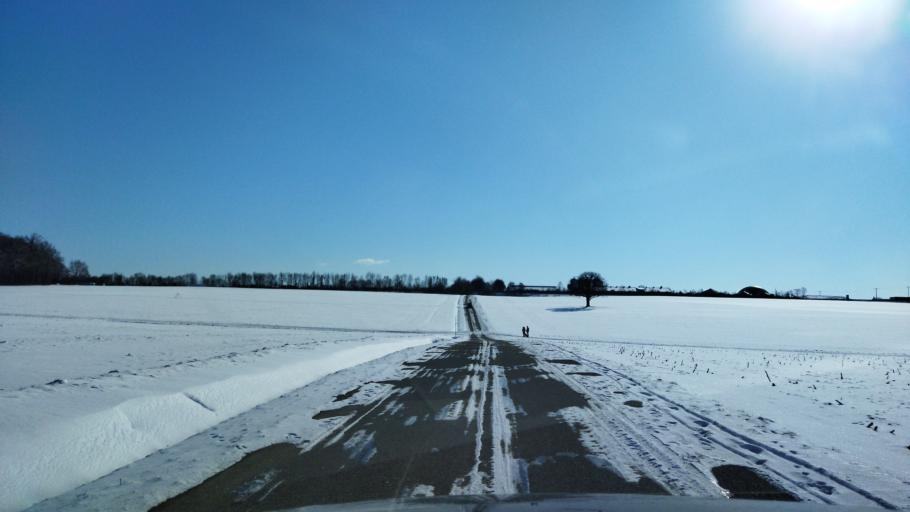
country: DE
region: Baden-Wuerttemberg
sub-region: Regierungsbezirk Stuttgart
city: Kirchberg an der Jagst
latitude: 49.1825
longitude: 9.9526
